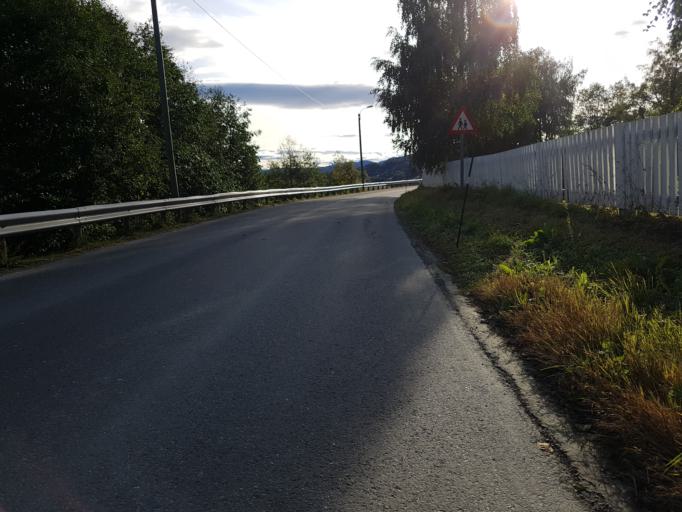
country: NO
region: Sor-Trondelag
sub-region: Klaebu
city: Klaebu
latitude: 63.3477
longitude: 10.4828
